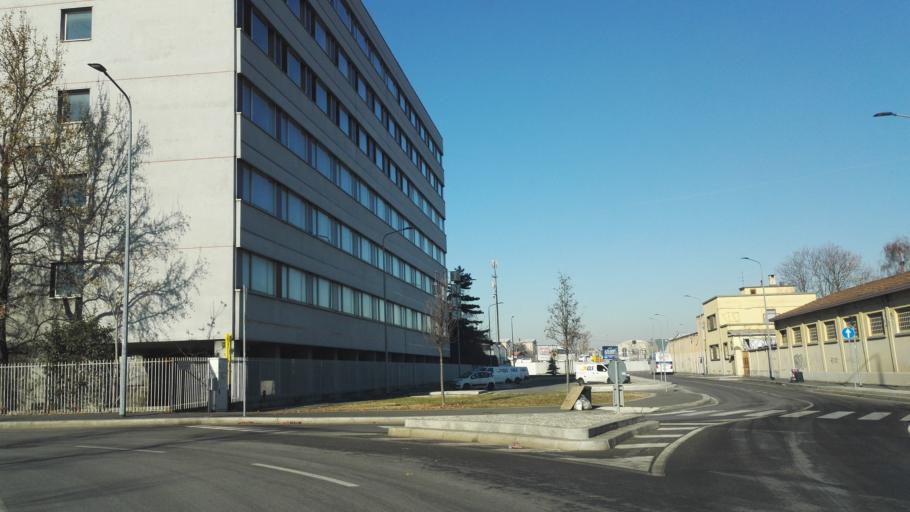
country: IT
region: Lombardy
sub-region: Citta metropolitana di Milano
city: Chiaravalle
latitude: 45.4440
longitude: 9.2320
